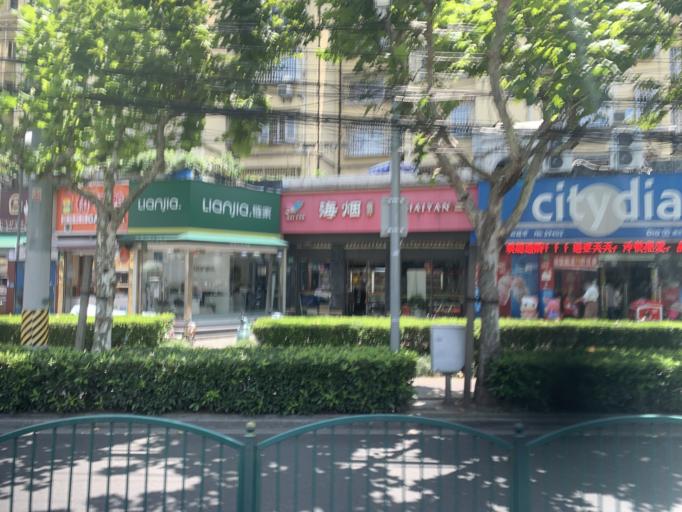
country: CN
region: Shanghai Shi
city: Pudong
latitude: 31.2509
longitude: 121.5756
